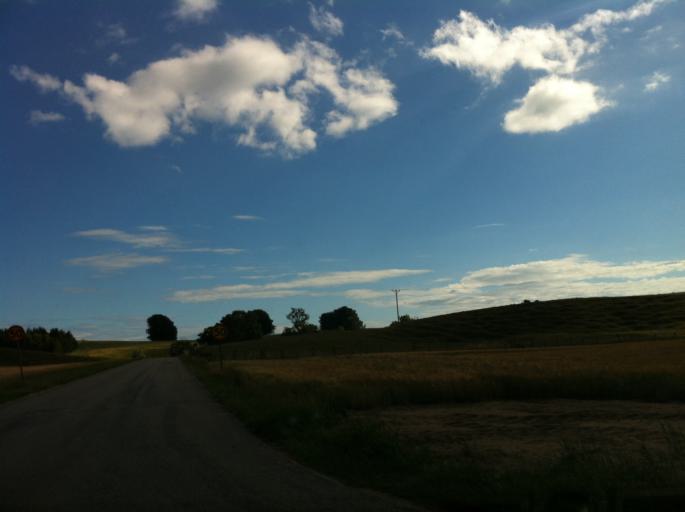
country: SE
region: Skane
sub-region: Ystads Kommun
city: Kopingebro
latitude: 55.3952
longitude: 14.0386
